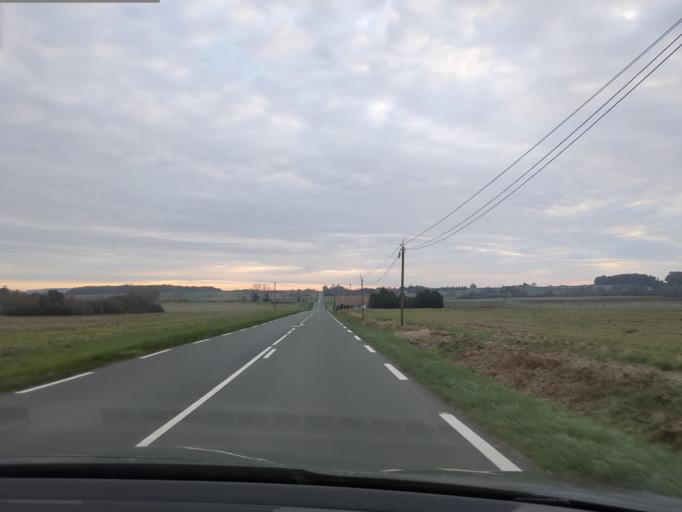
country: FR
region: Poitou-Charentes
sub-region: Departement de la Charente
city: Baignes-Sainte-Radegonde
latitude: 45.4481
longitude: -0.2742
